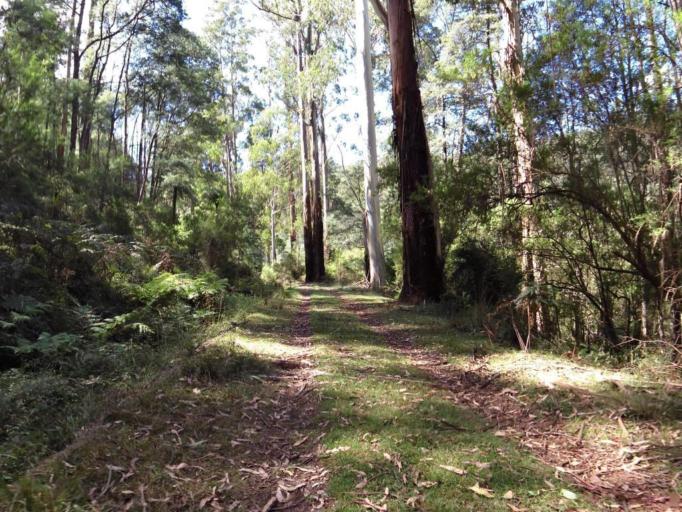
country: AU
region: Victoria
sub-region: Yarra Ranges
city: Millgrove
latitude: -37.6870
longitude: 145.8075
